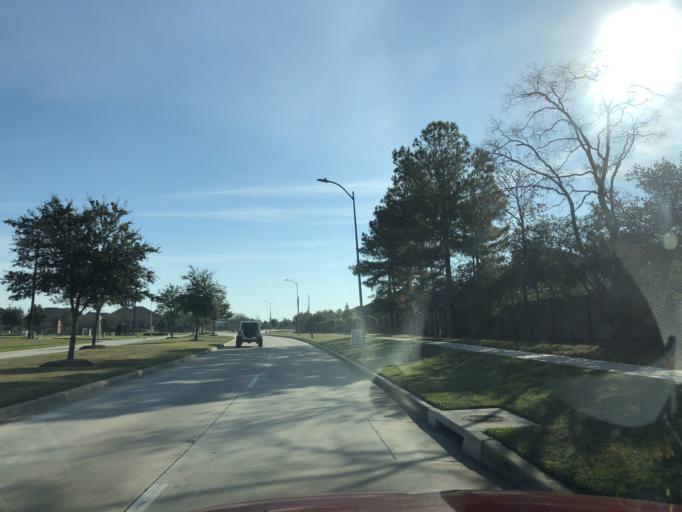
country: US
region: Texas
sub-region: Harris County
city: Tomball
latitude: 30.0552
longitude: -95.5740
